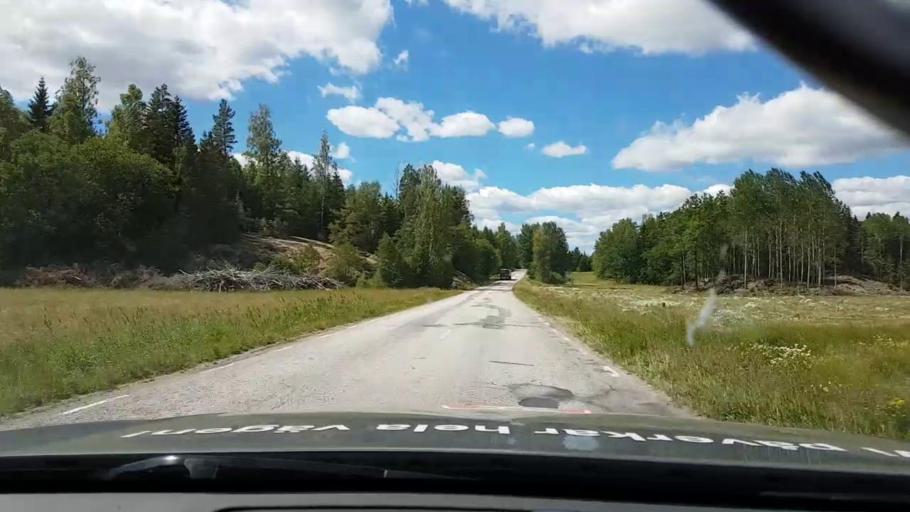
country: SE
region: Kalmar
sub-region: Vasterviks Kommun
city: Forserum
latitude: 58.0255
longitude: 16.5616
